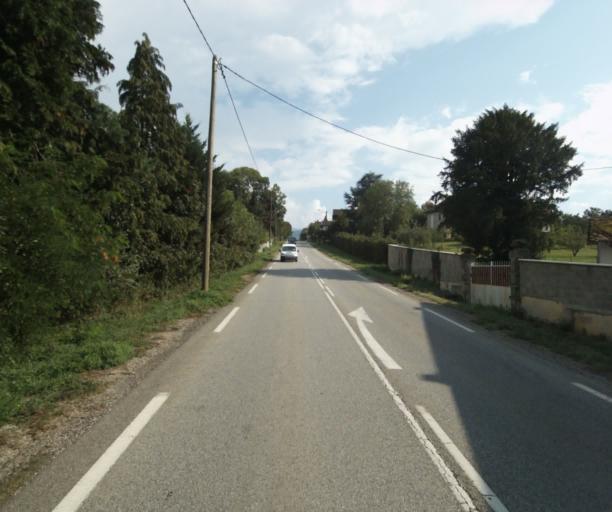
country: FR
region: Rhone-Alpes
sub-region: Departement de l'Isere
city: Brie-et-Angonnes
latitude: 45.1305
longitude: 5.7769
